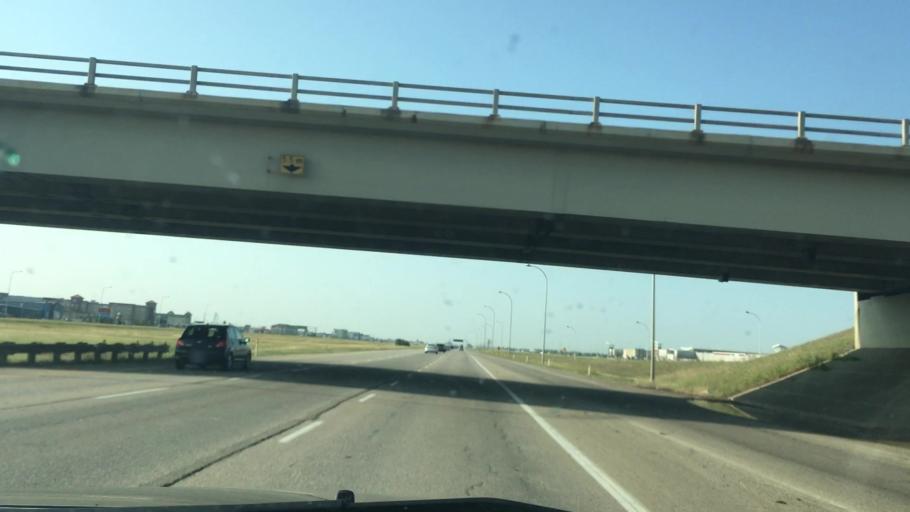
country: CA
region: Alberta
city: Leduc
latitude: 53.3090
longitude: -113.5499
